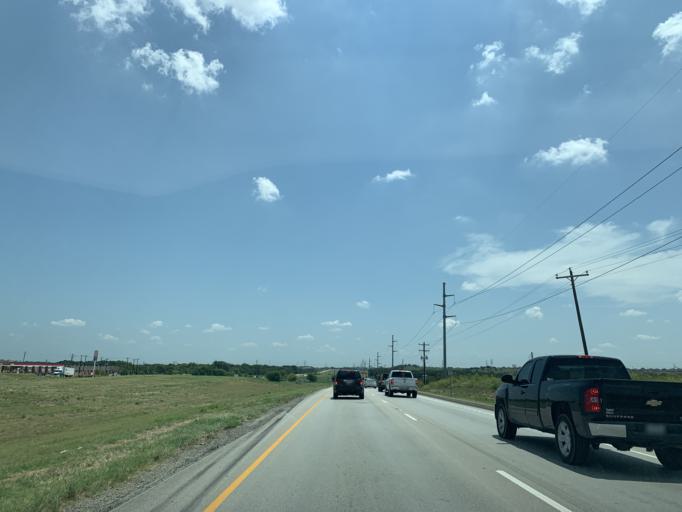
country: US
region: Texas
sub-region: Denton County
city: Roanoke
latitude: 33.0244
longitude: -97.2609
